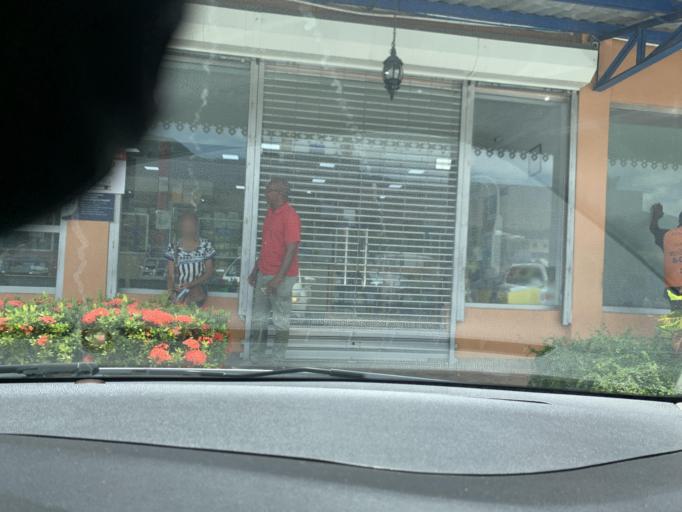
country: DO
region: Puerto Plata
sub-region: Puerto Plata
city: Puerto Plata
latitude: 19.7874
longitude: -70.6910
